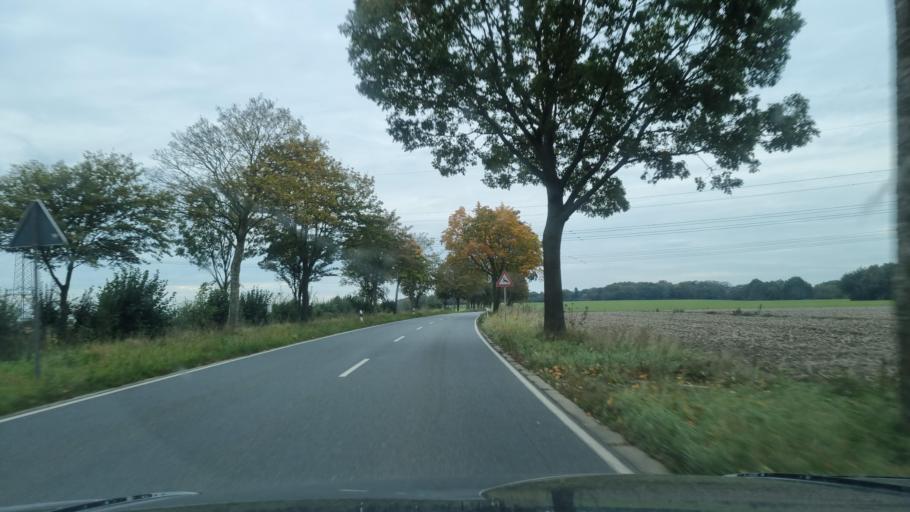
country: DE
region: North Rhine-Westphalia
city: Kalkar
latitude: 51.7133
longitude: 6.3072
